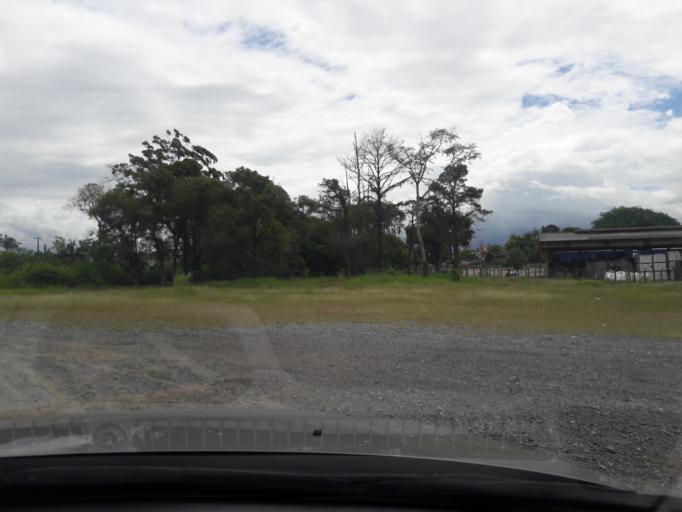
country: BR
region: Santa Catarina
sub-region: Joinville
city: Joinville
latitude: -26.3179
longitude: -48.8339
